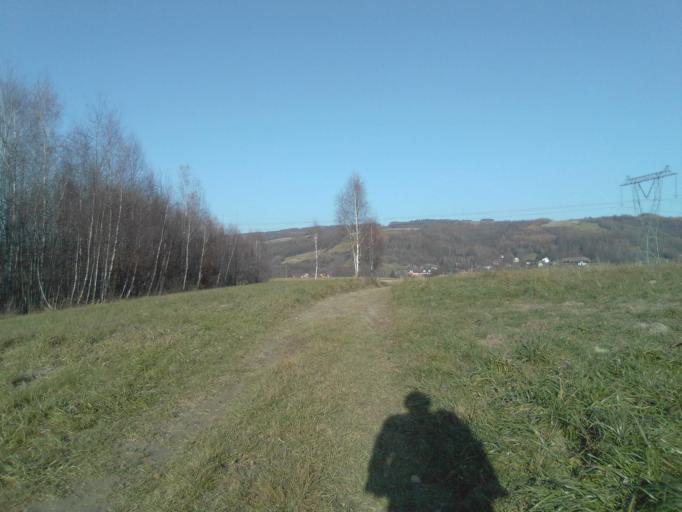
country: PL
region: Subcarpathian Voivodeship
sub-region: Powiat strzyzowski
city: Jawornik
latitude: 49.7981
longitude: 21.8857
